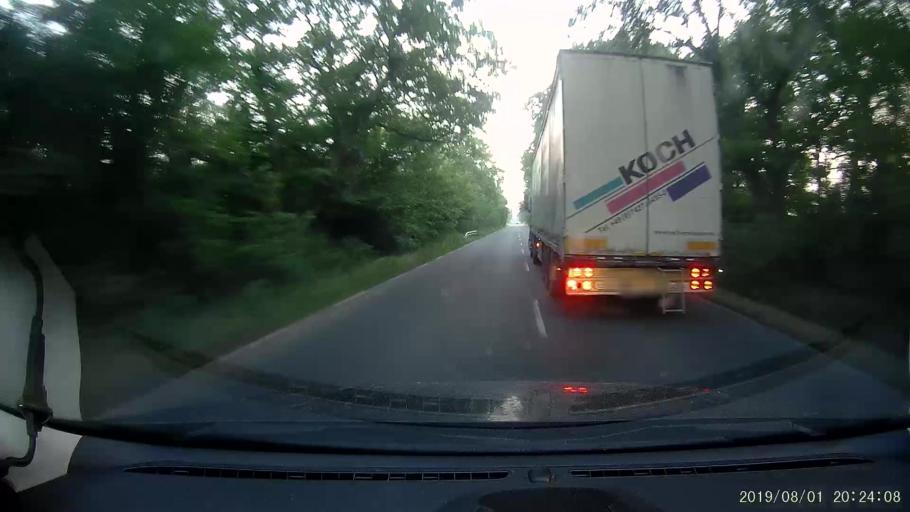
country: BG
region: Yambol
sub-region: Obshtina Elkhovo
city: Elkhovo
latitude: 42.2369
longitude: 26.5956
